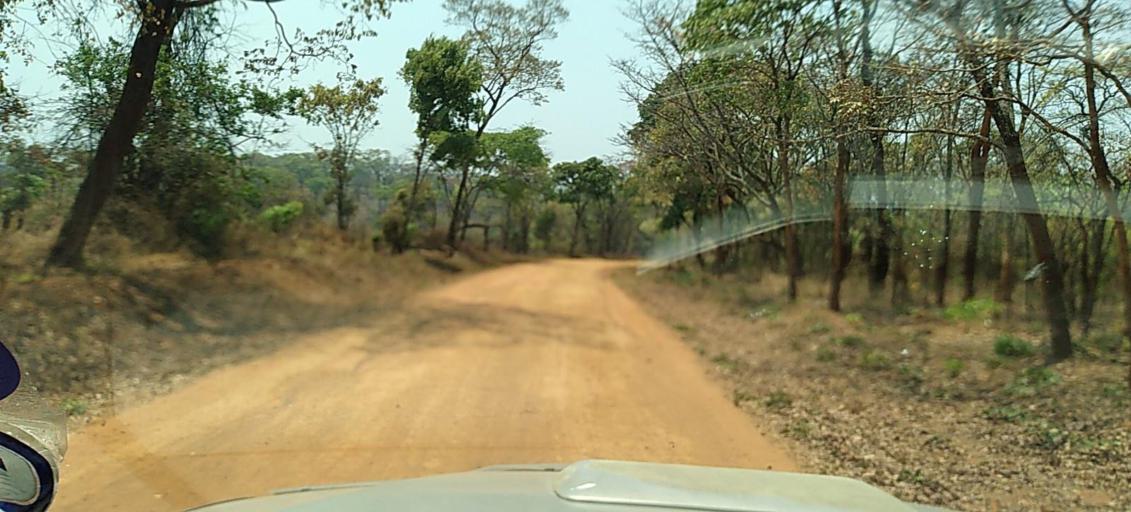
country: ZM
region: North-Western
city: Kasempa
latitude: -13.5452
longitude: 26.0401
